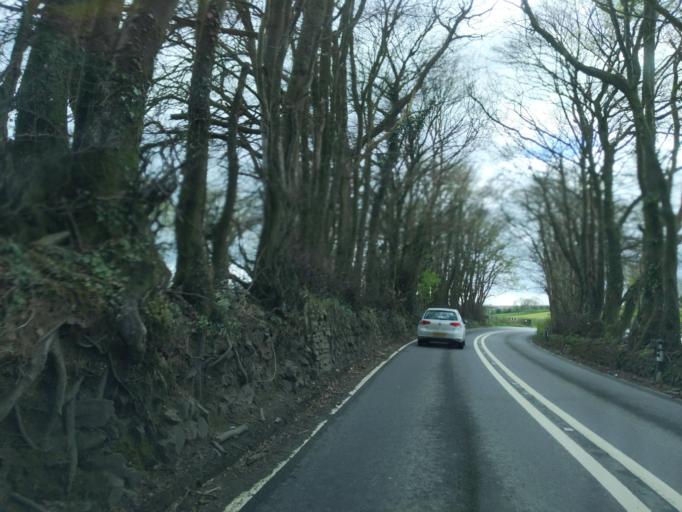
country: GB
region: England
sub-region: Cornwall
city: Callington
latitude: 50.4883
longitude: -4.3473
